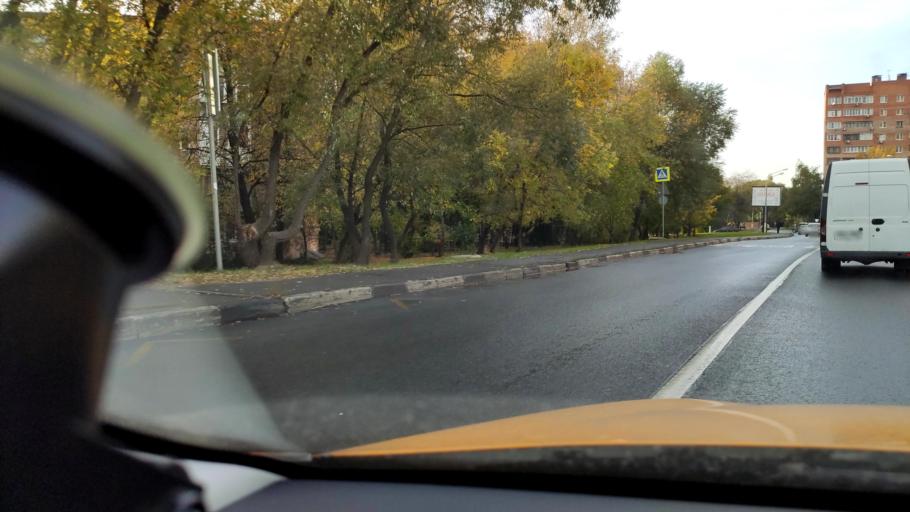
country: RU
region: Moskovskaya
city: Mytishchi
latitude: 55.9176
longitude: 37.7322
